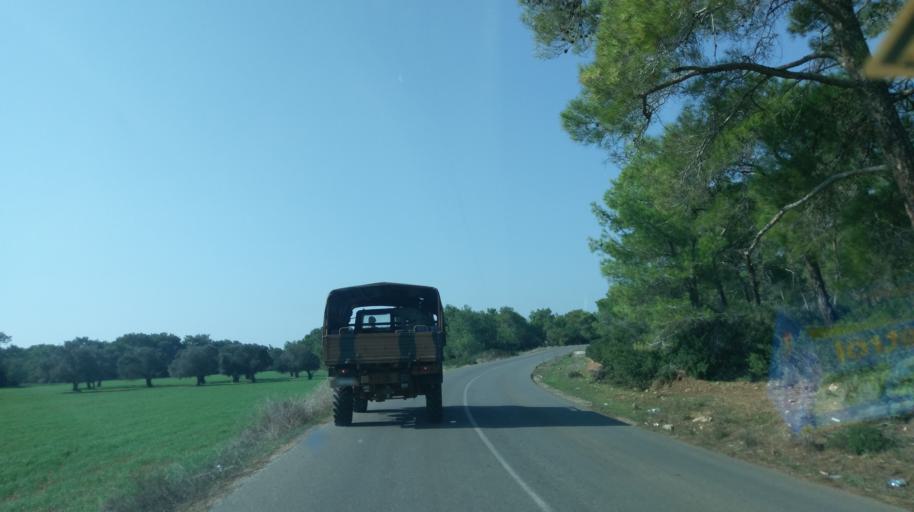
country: CY
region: Lefkosia
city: Morfou
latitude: 35.3034
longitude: 33.0296
